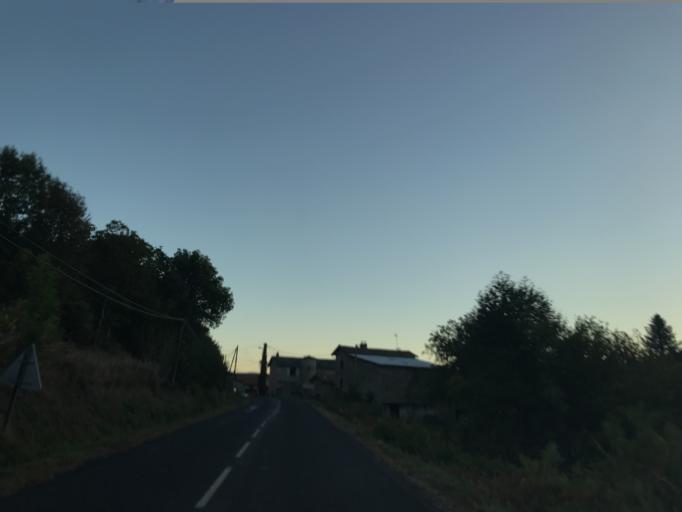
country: FR
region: Auvergne
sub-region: Departement du Puy-de-Dome
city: Celles-sur-Durolle
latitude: 45.8448
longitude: 3.6349
